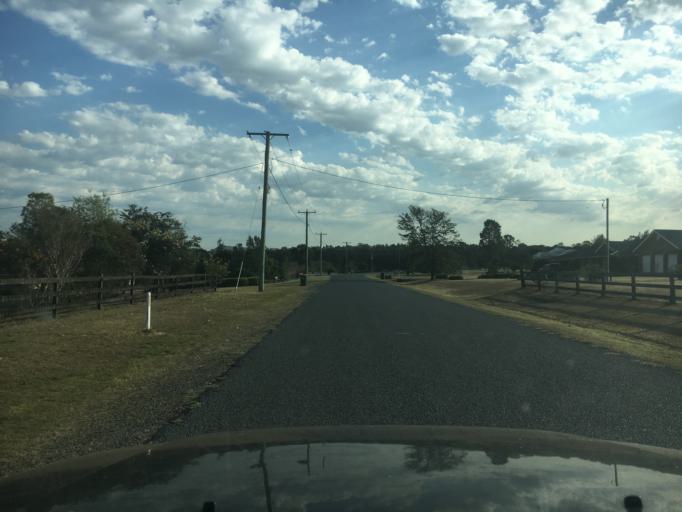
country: AU
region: New South Wales
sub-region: Cessnock
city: Branxton
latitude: -32.6515
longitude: 151.3701
